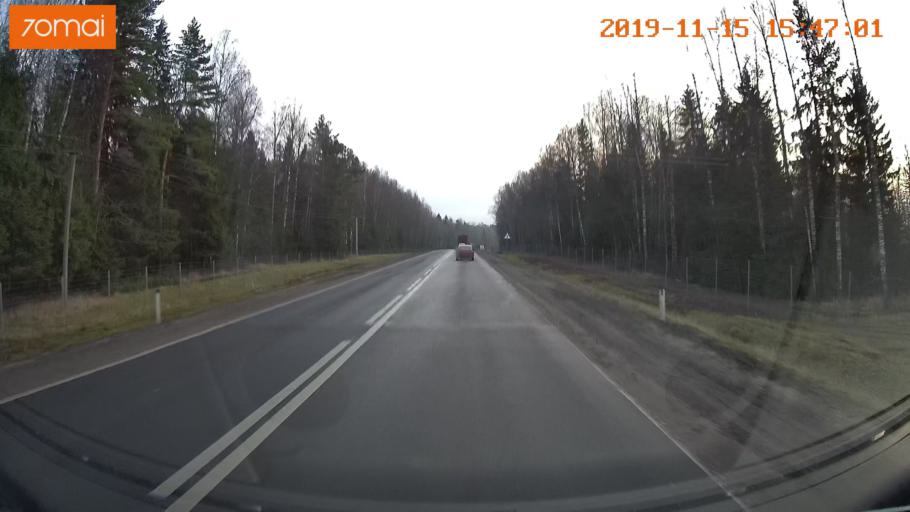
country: RU
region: Jaroslavl
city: Danilov
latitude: 57.9431
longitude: 40.0121
